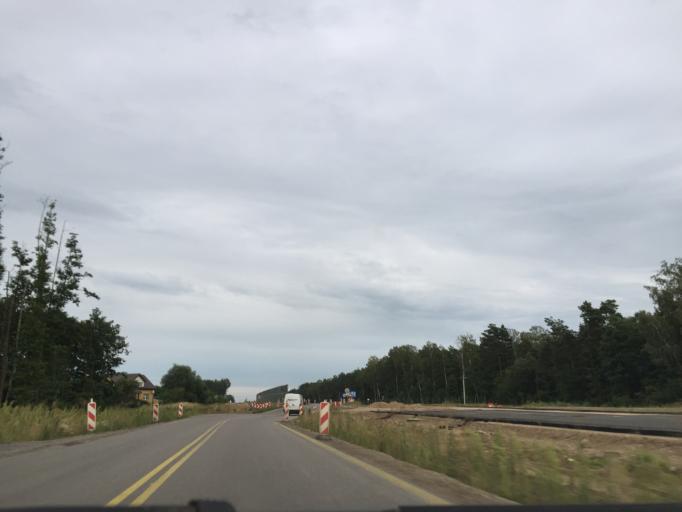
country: PL
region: Podlasie
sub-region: Powiat bialostocki
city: Tykocin
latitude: 53.1284
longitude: 22.6991
